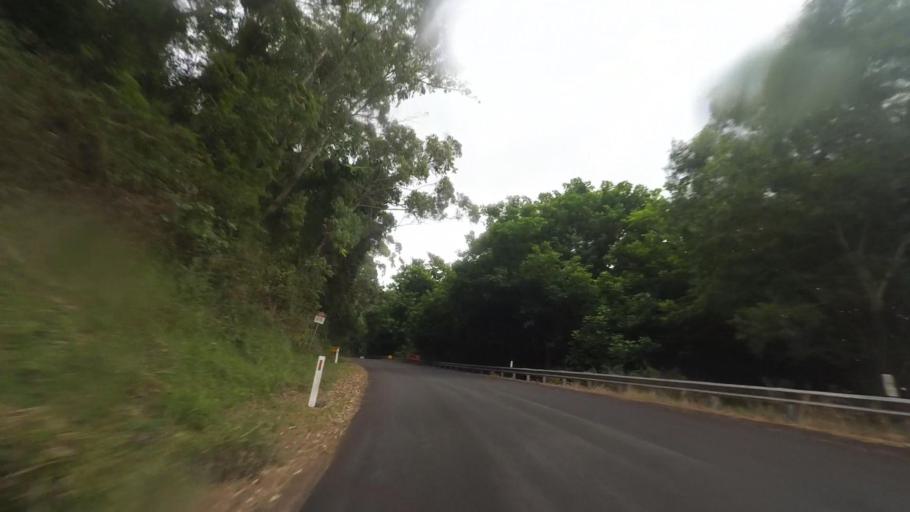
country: AU
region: New South Wales
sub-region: Wollongong
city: Cordeaux Heights
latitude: -34.4214
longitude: 150.8167
